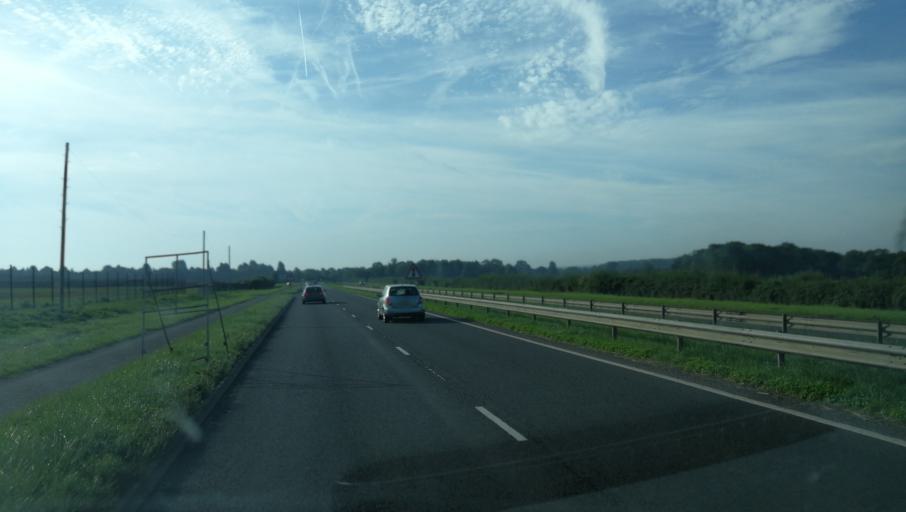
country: GB
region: England
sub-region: Oxfordshire
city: Yarnton
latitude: 51.8316
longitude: -1.3252
